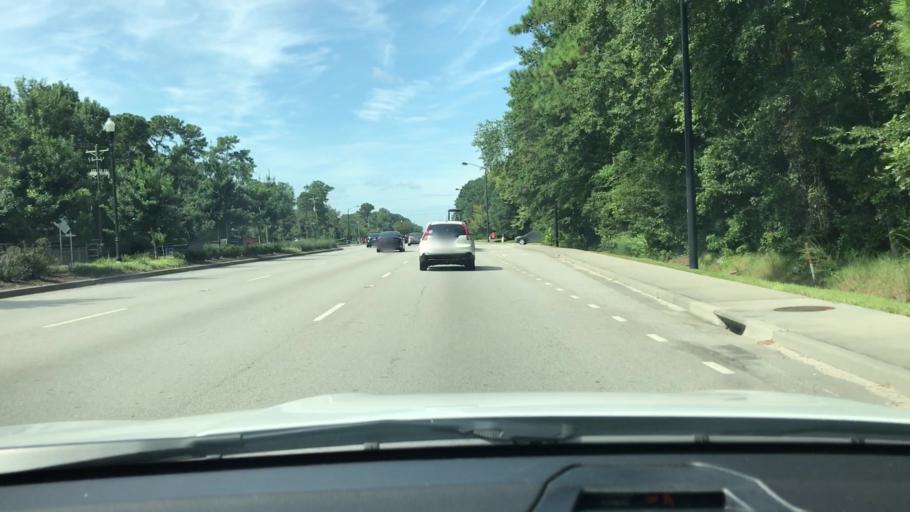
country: US
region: South Carolina
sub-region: Charleston County
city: Isle of Palms
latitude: 32.8535
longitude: -79.8030
